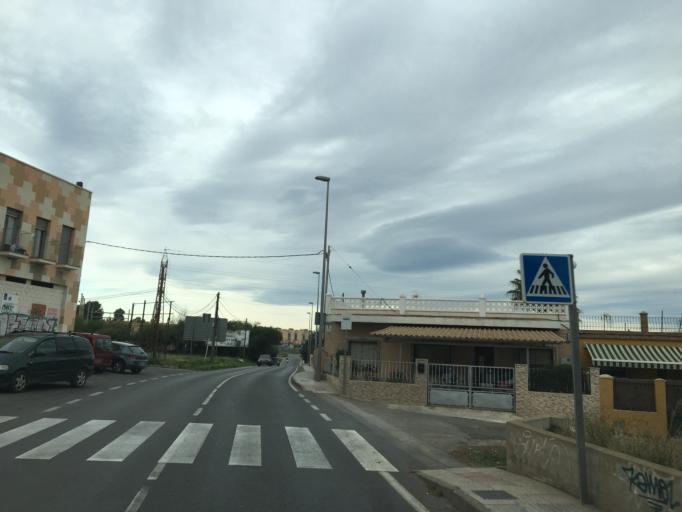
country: ES
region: Murcia
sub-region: Murcia
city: Cartagena
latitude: 37.6129
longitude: -1.0130
